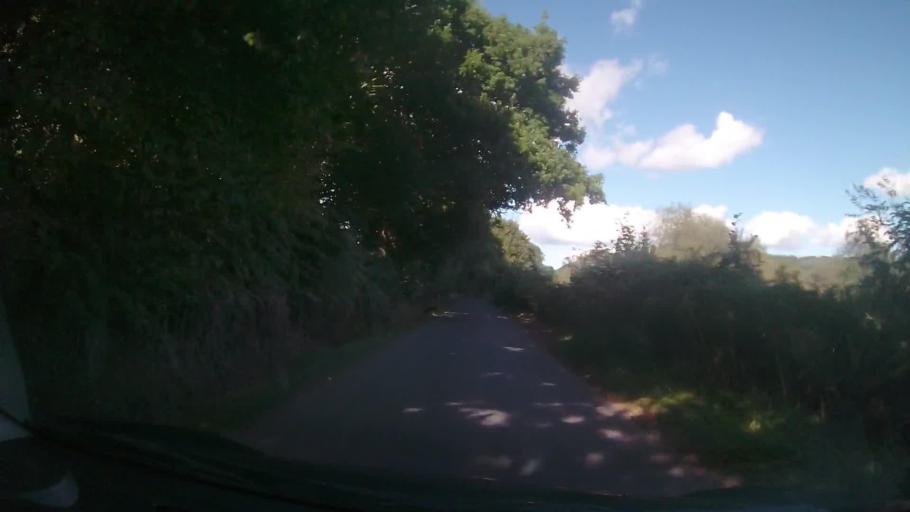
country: GB
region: Wales
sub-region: Sir Powys
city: Brecon
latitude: 51.8736
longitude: -3.3073
